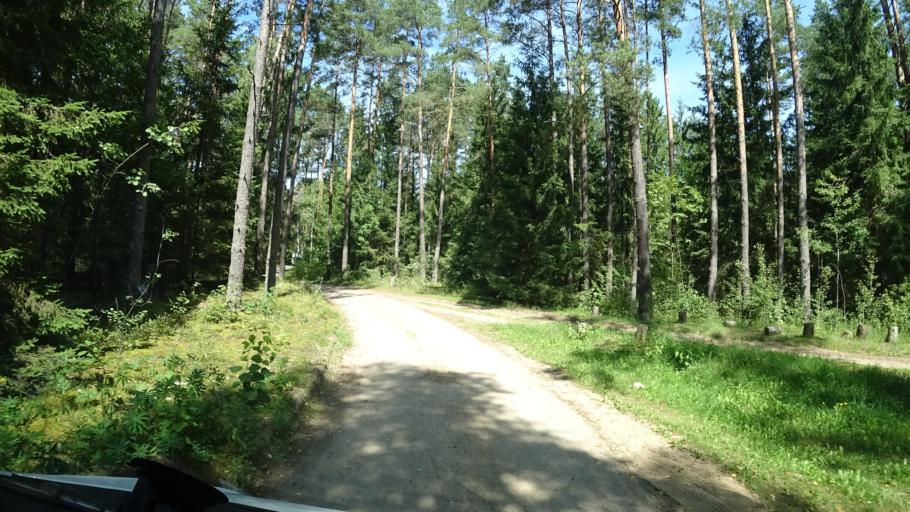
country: LT
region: Vilnius County
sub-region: Trakai
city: Rudiskes
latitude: 54.5086
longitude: 24.8898
